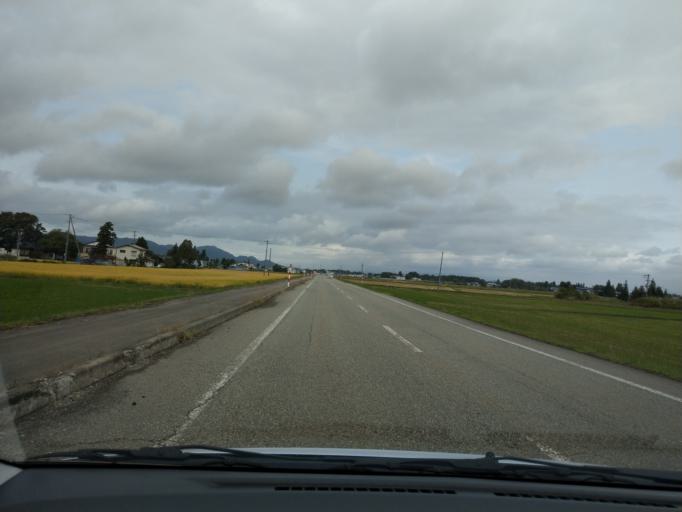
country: JP
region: Akita
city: Omagari
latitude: 39.3882
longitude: 140.4854
